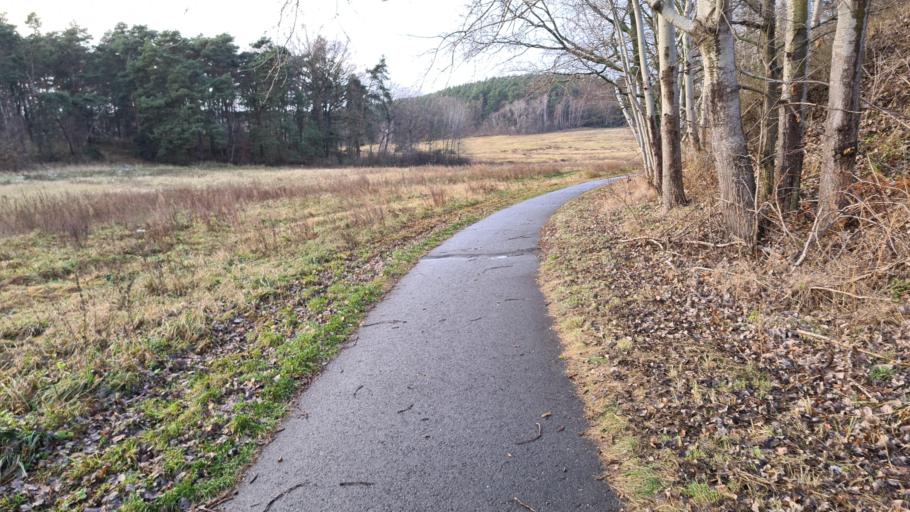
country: DE
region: Brandenburg
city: Groden
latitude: 51.3965
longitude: 13.5842
